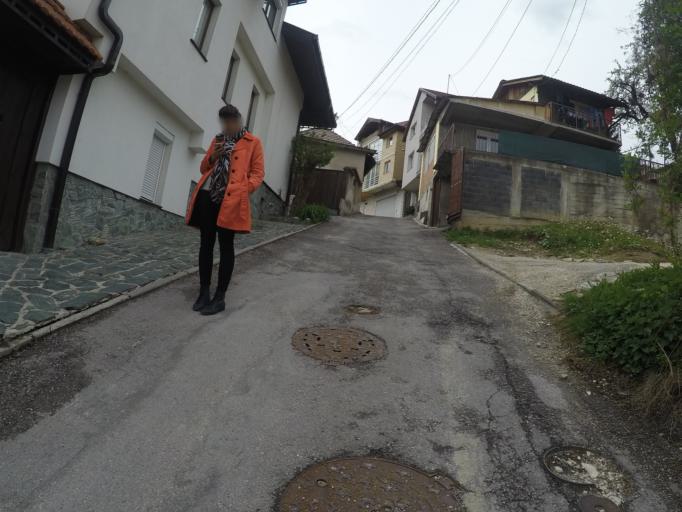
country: BA
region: Federation of Bosnia and Herzegovina
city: Kobilja Glava
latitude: 43.8521
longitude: 18.4279
